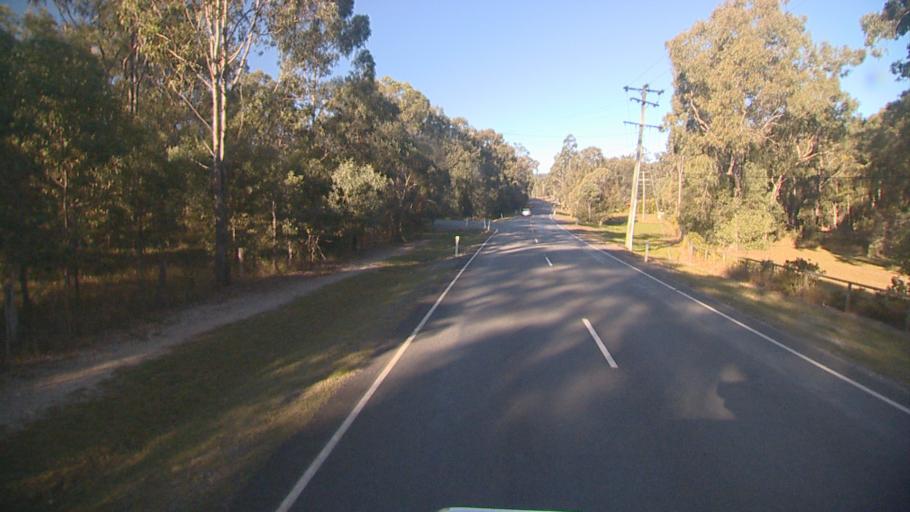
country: AU
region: Queensland
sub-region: Logan
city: Chambers Flat
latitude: -27.7693
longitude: 153.1317
